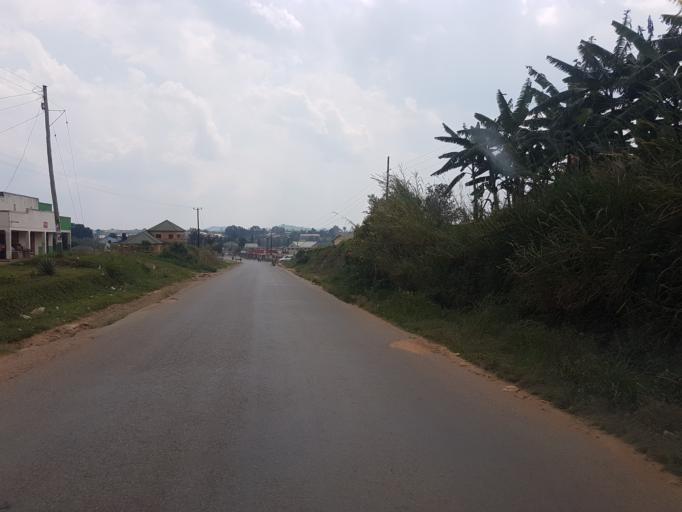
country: UG
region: Western Region
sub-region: Bushenyi District
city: Bushenyi
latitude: -0.5422
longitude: 30.1322
